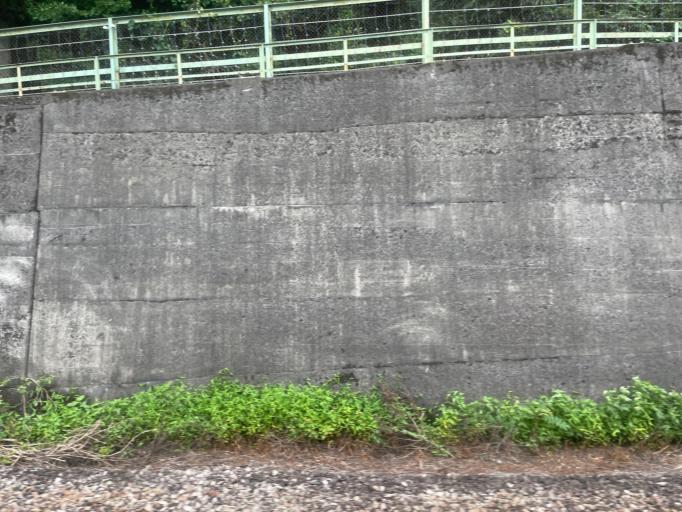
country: JP
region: Gunma
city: Shibukawa
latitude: 36.5102
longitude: 139.0240
